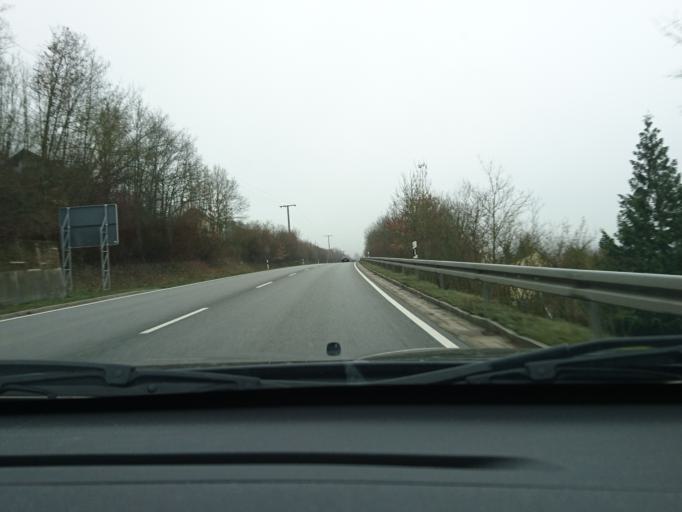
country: DE
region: Bavaria
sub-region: Regierungsbezirk Unterfranken
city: Neuendorf
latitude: 50.0626
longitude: 9.6501
